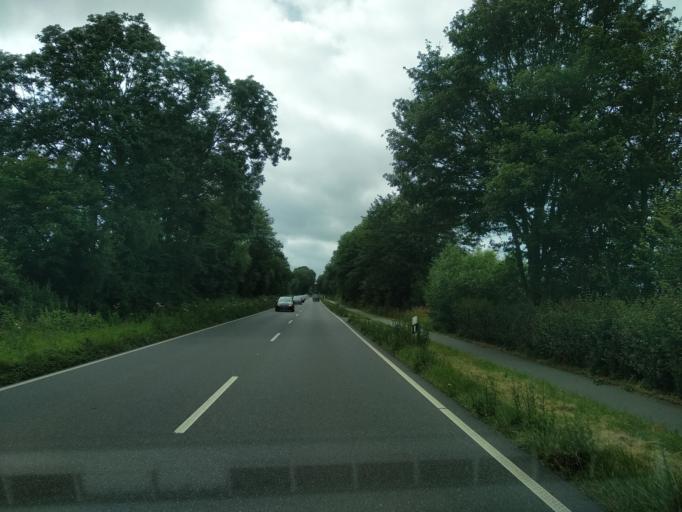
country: DE
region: Schleswig-Holstein
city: Ringsberg
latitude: 54.8063
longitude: 9.5858
